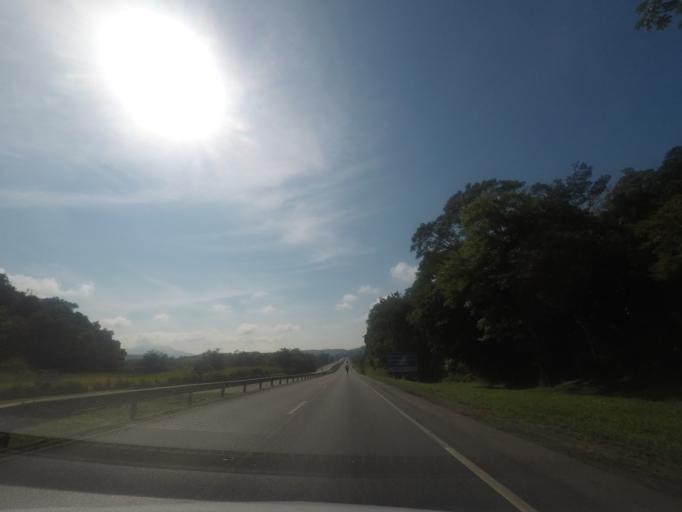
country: BR
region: Parana
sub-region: Antonina
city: Antonina
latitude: -25.5331
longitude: -48.7556
